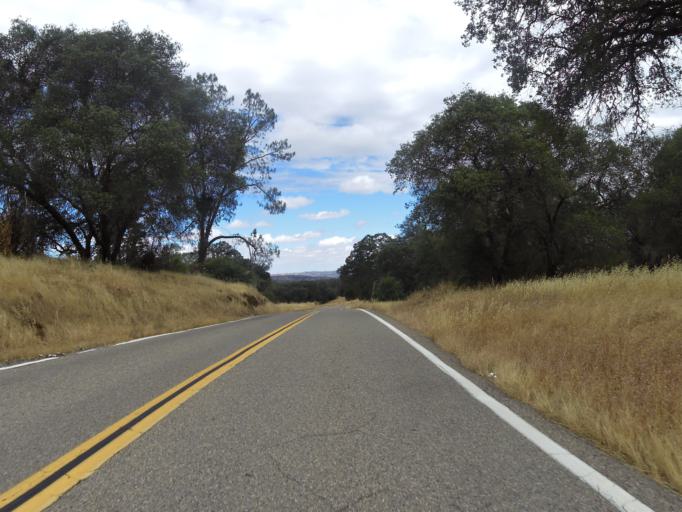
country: US
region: California
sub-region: Madera County
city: Yosemite Lakes
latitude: 37.2411
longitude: -119.8354
